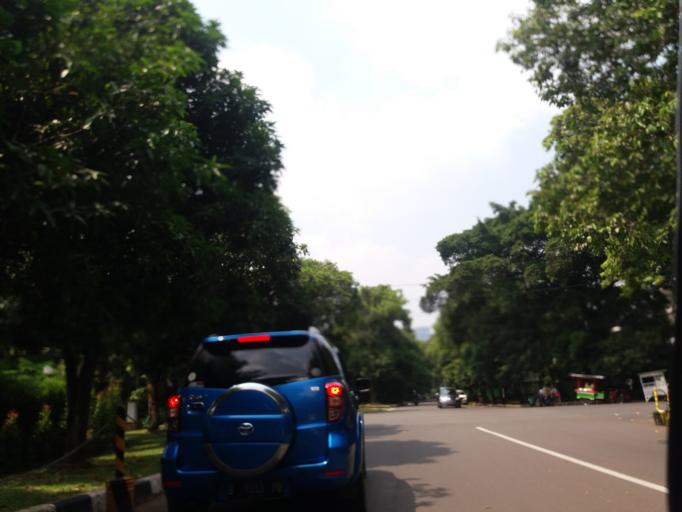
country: ID
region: Jakarta Raya
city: Jakarta
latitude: -6.2326
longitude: 106.8030
